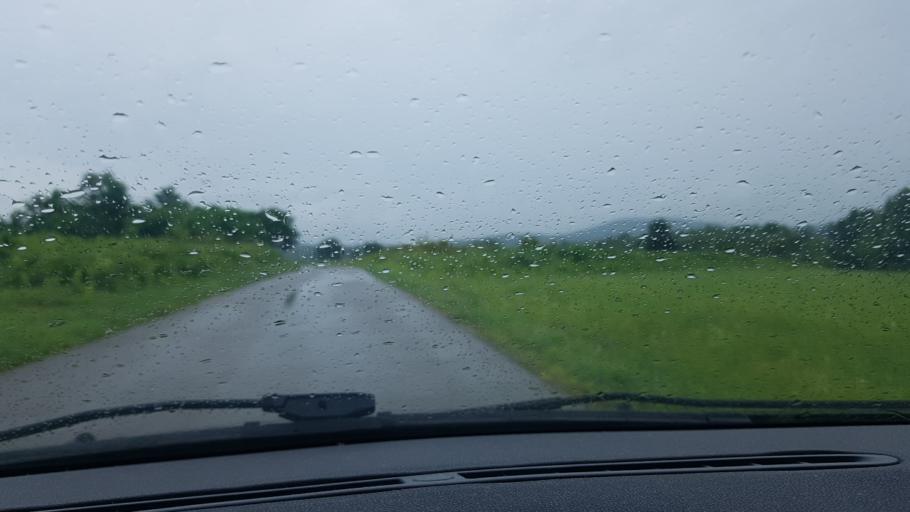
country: HR
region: Licko-Senjska
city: Jezerce
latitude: 44.9899
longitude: 15.6646
